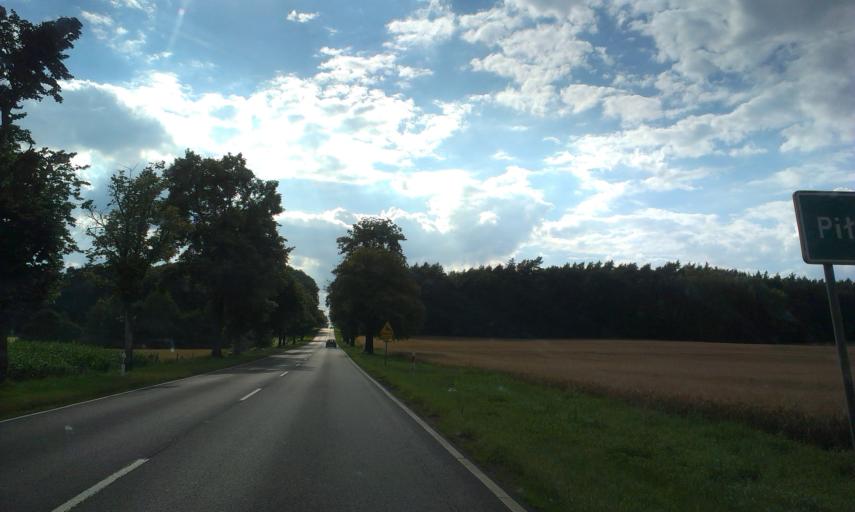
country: PL
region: Greater Poland Voivodeship
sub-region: Powiat pilski
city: Miasteczko Krajenskie
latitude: 53.1329
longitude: 16.9932
